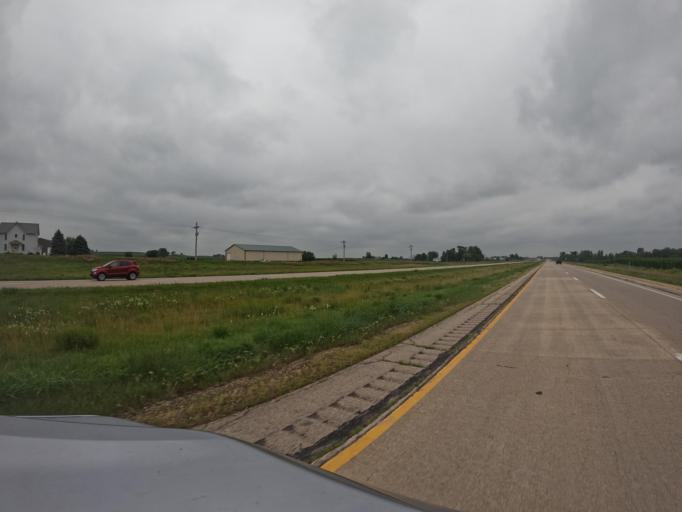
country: US
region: Iowa
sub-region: Clinton County
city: De Witt
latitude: 41.8859
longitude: -90.5839
